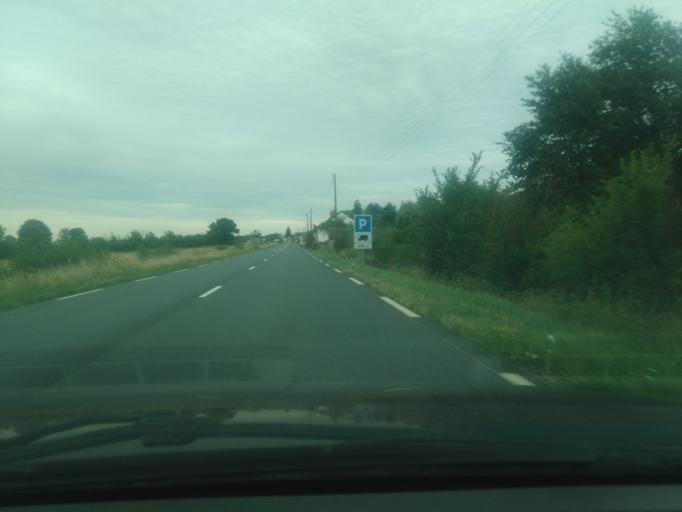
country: FR
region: Centre
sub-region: Departement de l'Indre
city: Arthon
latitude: 46.6143
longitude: 1.6793
